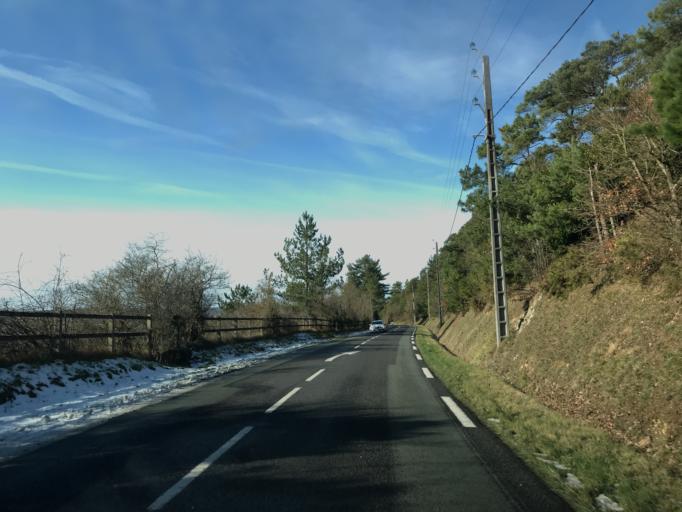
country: FR
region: Haute-Normandie
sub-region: Departement de l'Eure
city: Houlbec-Cocherel
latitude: 49.0641
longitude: 1.3219
